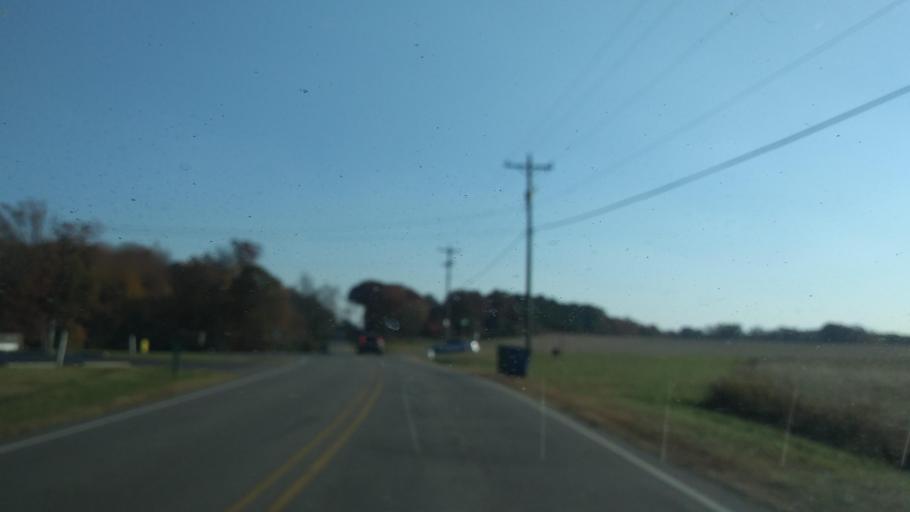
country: US
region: North Carolina
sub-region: Rockingham County
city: Reidsville
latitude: 36.2498
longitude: -79.7229
